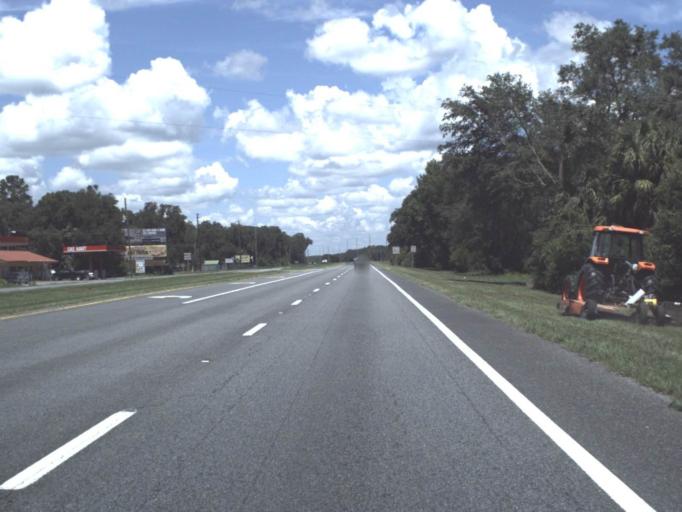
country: US
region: Florida
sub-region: Dixie County
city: Cross City
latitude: 29.6120
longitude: -83.0881
